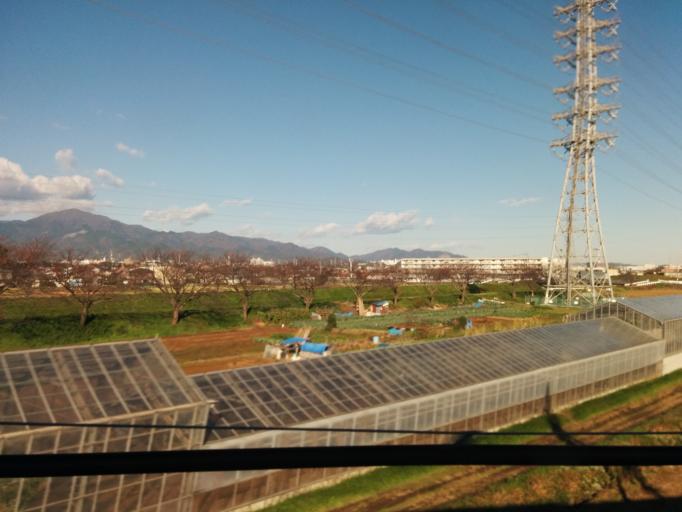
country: JP
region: Kanagawa
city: Isehara
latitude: 35.3750
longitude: 139.3473
